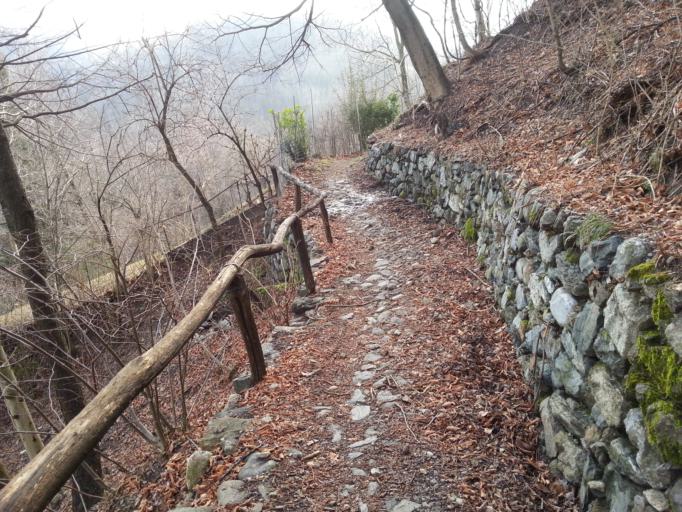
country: IT
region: Lombardy
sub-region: Provincia di Como
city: Plesio
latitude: 46.0557
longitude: 9.2355
